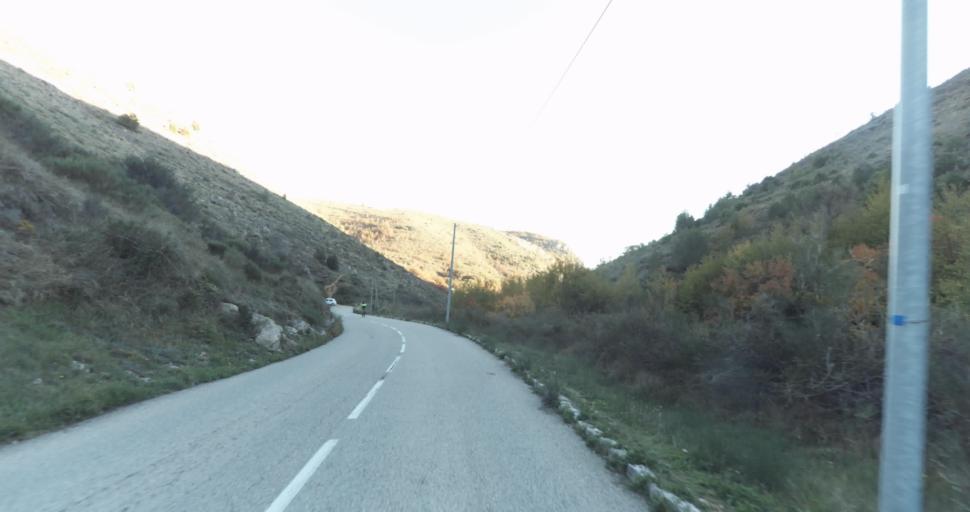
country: FR
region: Provence-Alpes-Cote d'Azur
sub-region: Departement des Alpes-Maritimes
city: Vence
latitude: 43.7444
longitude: 7.1029
